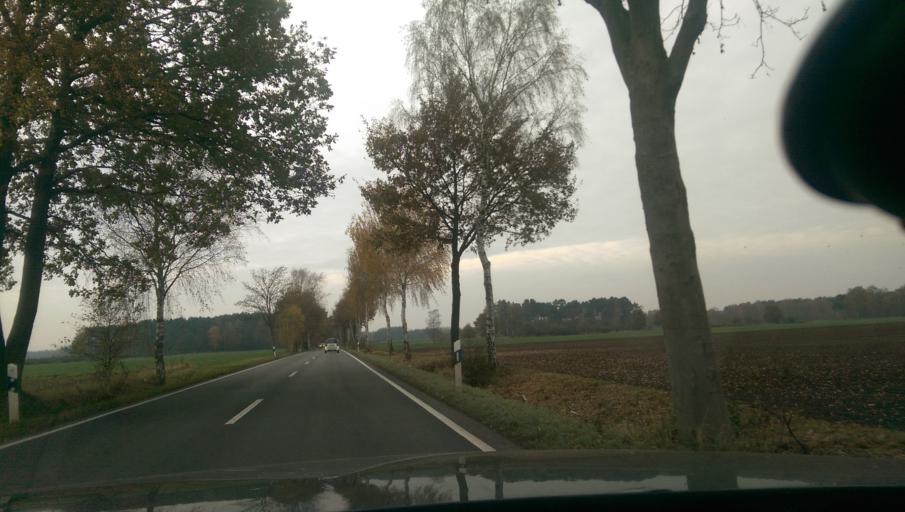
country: DE
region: Lower Saxony
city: Lindwedel
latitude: 52.5403
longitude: 9.6223
